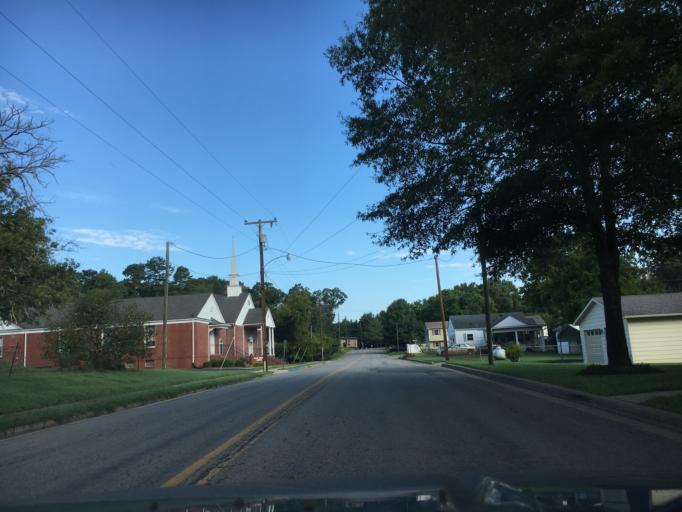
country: US
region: Virginia
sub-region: Halifax County
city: South Boston
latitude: 36.7028
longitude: -78.9112
